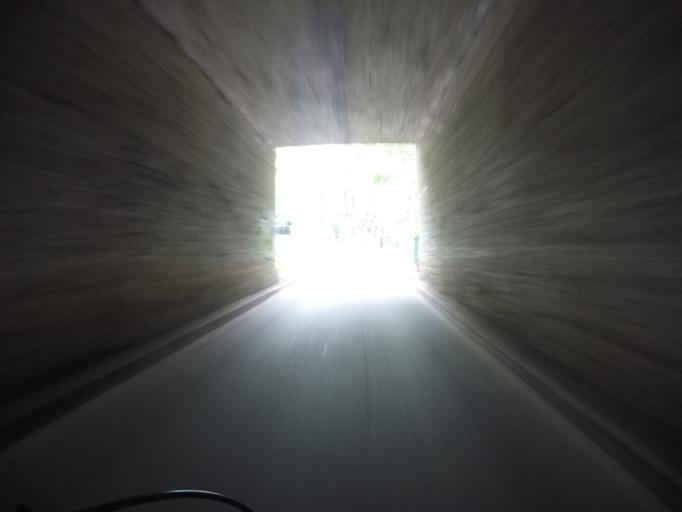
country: DE
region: Brandenburg
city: Potsdam
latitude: 52.3714
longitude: 13.0134
